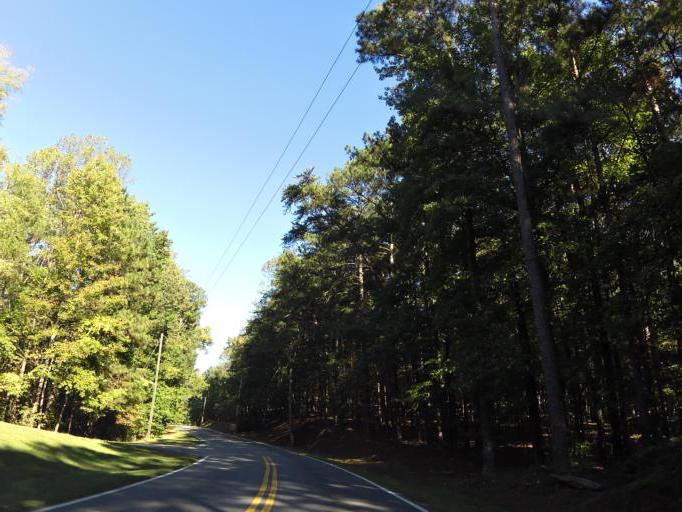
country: US
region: Georgia
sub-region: Bartow County
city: Emerson
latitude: 34.1464
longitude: -84.7170
